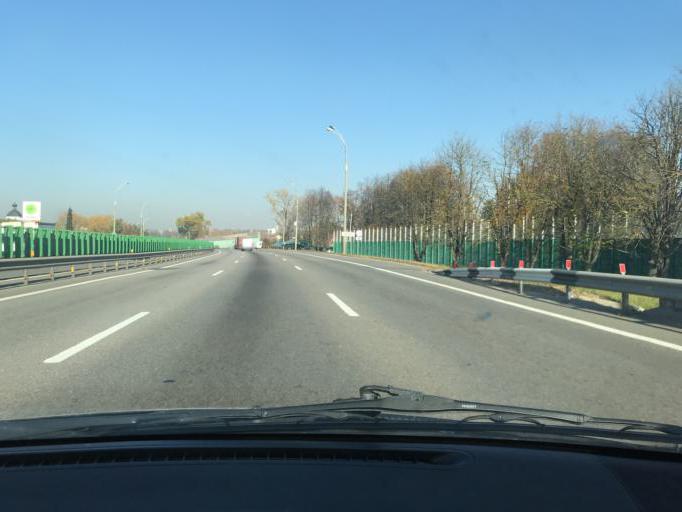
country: BY
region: Minsk
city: Syenitsa
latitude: 53.8237
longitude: 27.5336
